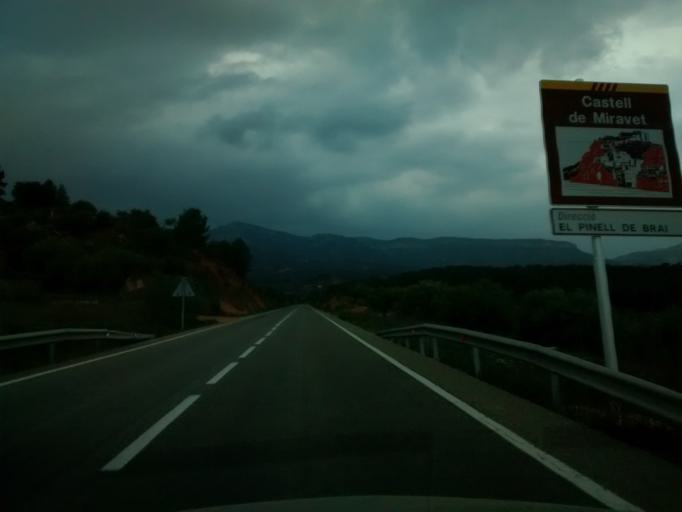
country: ES
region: Catalonia
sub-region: Provincia de Tarragona
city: Benifallet
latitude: 41.0044
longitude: 0.5114
